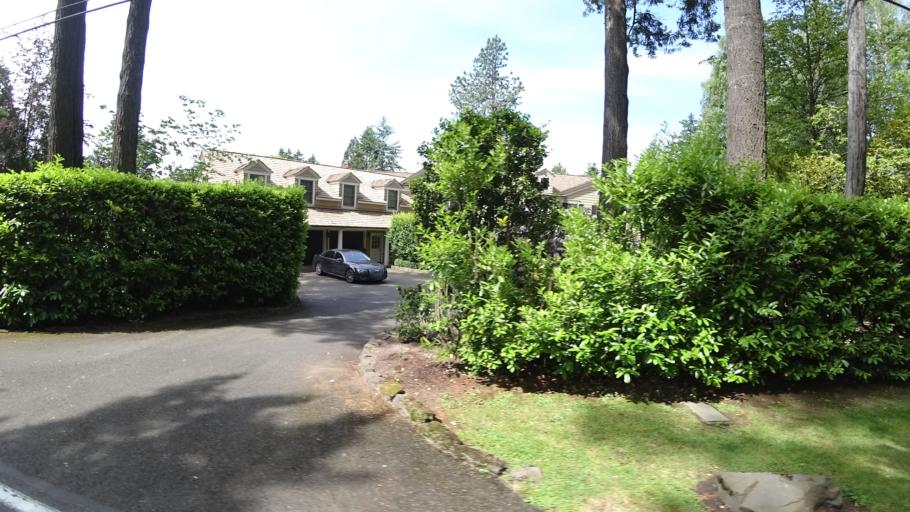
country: US
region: Oregon
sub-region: Clackamas County
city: Lake Oswego
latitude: 45.4435
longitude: -122.6681
